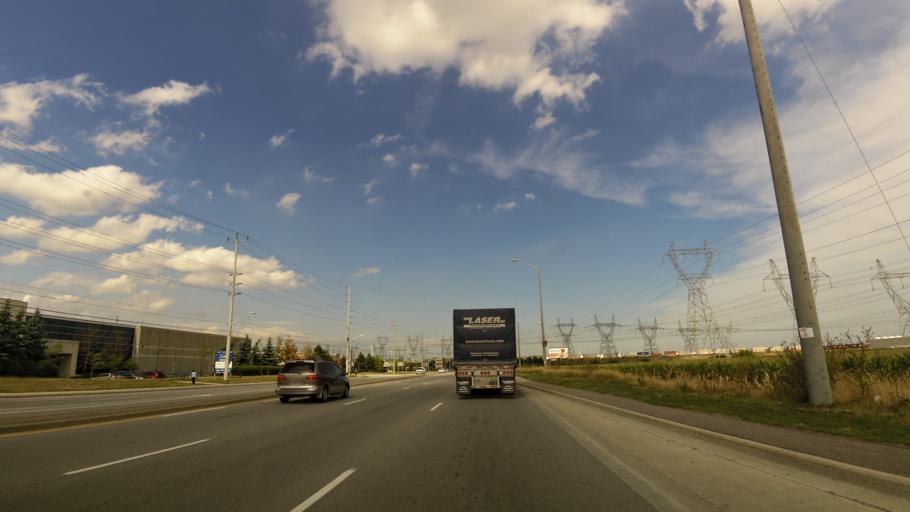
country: CA
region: Ontario
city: Brampton
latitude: 43.7247
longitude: -79.6678
